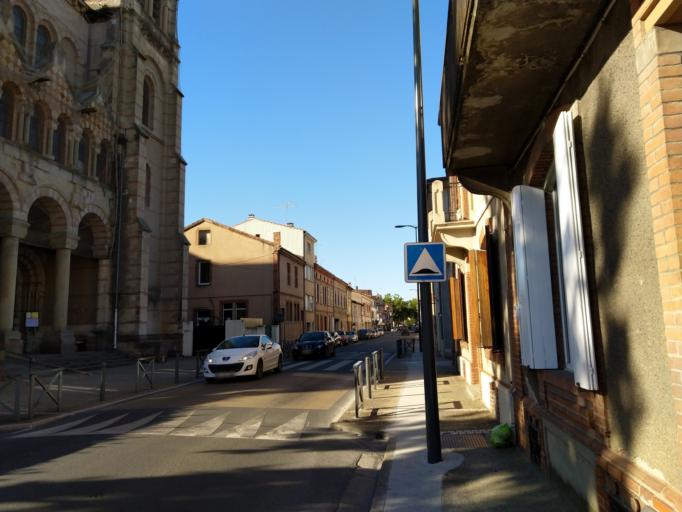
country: FR
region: Midi-Pyrenees
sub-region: Departement du Tarn
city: Albi
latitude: 43.9236
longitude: 2.1504
